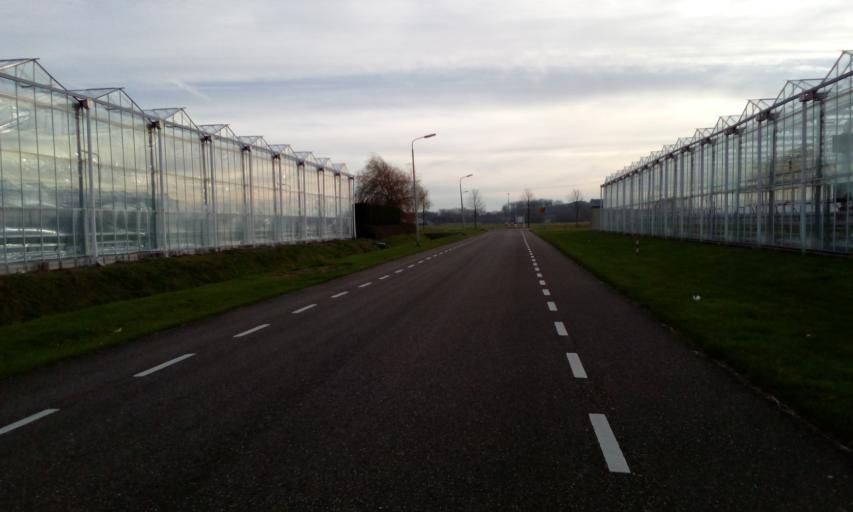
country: NL
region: South Holland
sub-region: Gemeente Lansingerland
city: Bleiswijk
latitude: 51.9852
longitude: 4.5340
